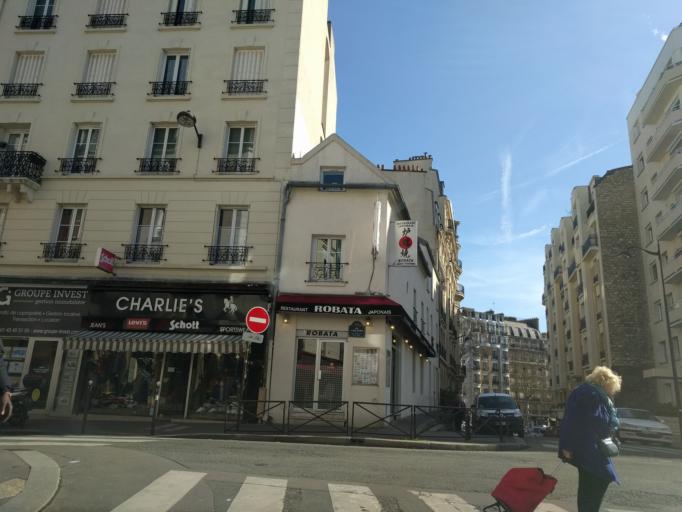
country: FR
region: Ile-de-France
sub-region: Departement du Val-de-Marne
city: Saint-Mande
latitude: 48.8386
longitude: 2.3961
